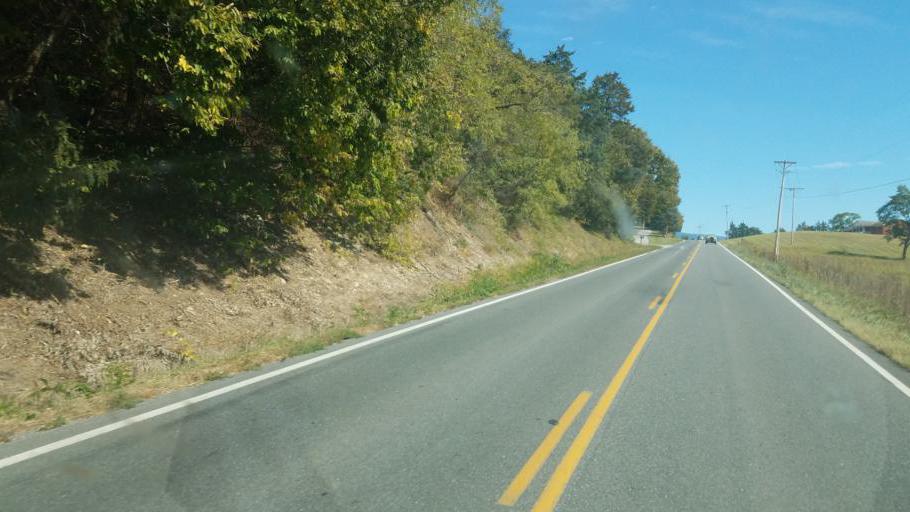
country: US
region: Virginia
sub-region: Page County
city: Stanley
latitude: 38.5896
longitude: -78.5788
